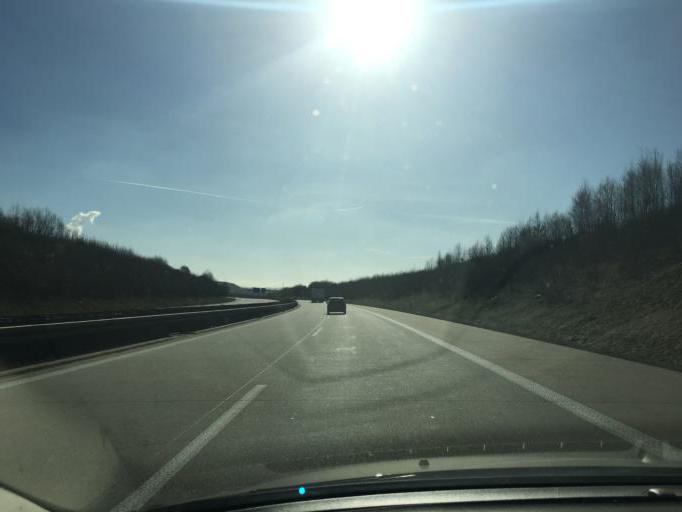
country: DE
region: Saxony
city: Hartmannsdorf
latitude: 50.8561
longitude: 12.8251
